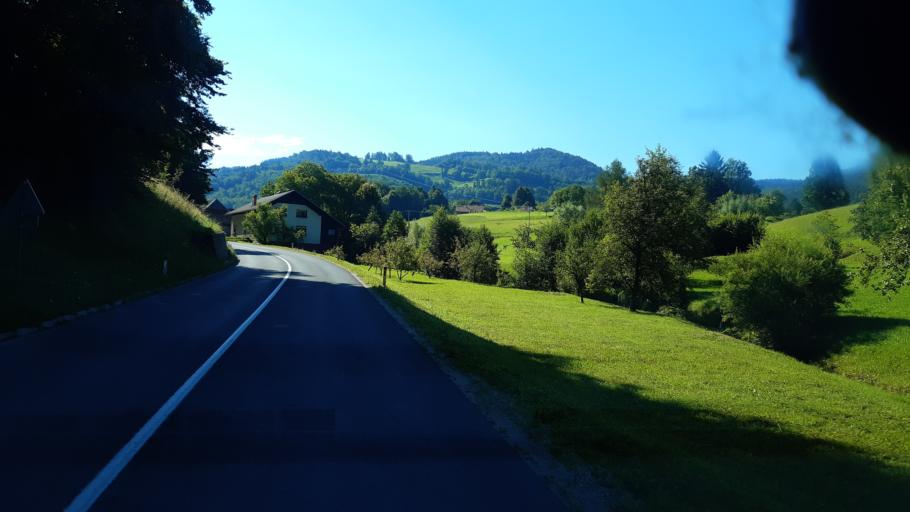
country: SI
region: Gornji Grad
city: Gornji Grad
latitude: 46.2214
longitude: 14.7848
